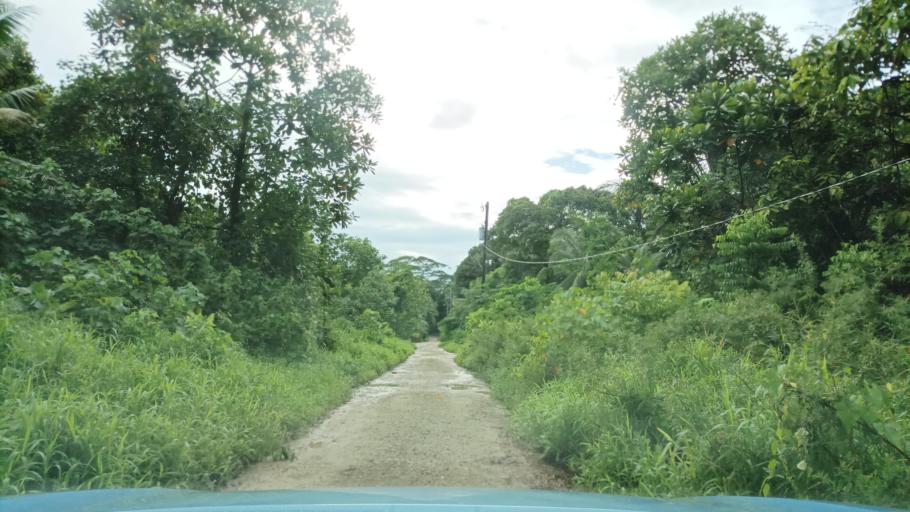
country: FM
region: Pohnpei
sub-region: Sokehs Municipality
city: Palikir - National Government Center
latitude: 6.8809
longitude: 158.1703
